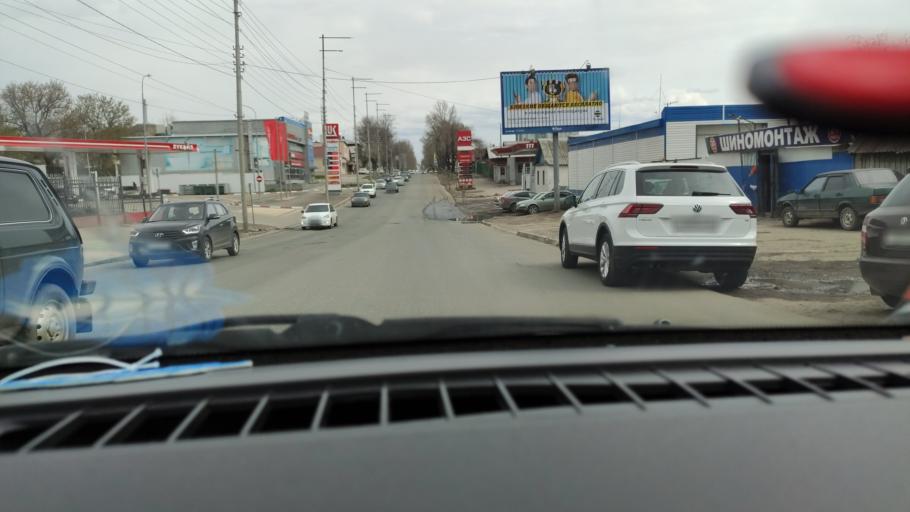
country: RU
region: Saratov
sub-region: Saratovskiy Rayon
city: Saratov
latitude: 51.5436
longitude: 46.0350
